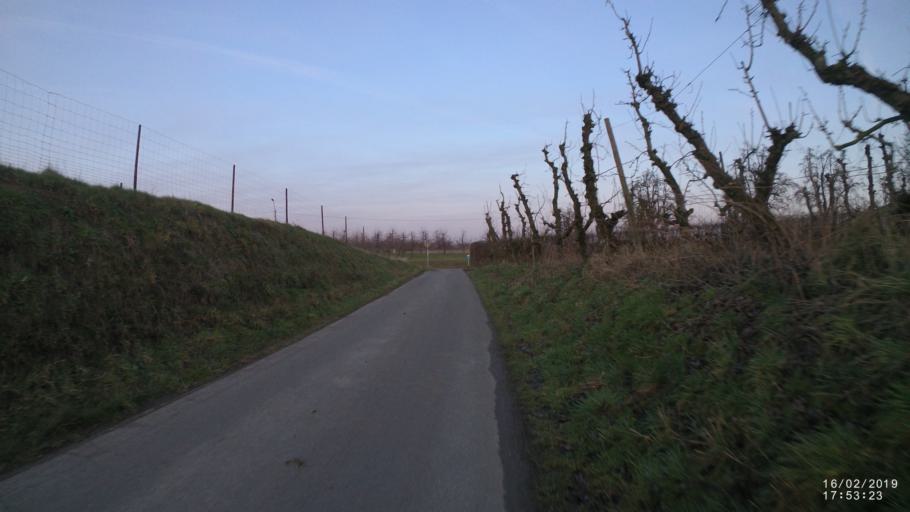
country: BE
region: Flanders
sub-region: Provincie Limburg
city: Sint-Truiden
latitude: 50.8158
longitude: 5.1564
